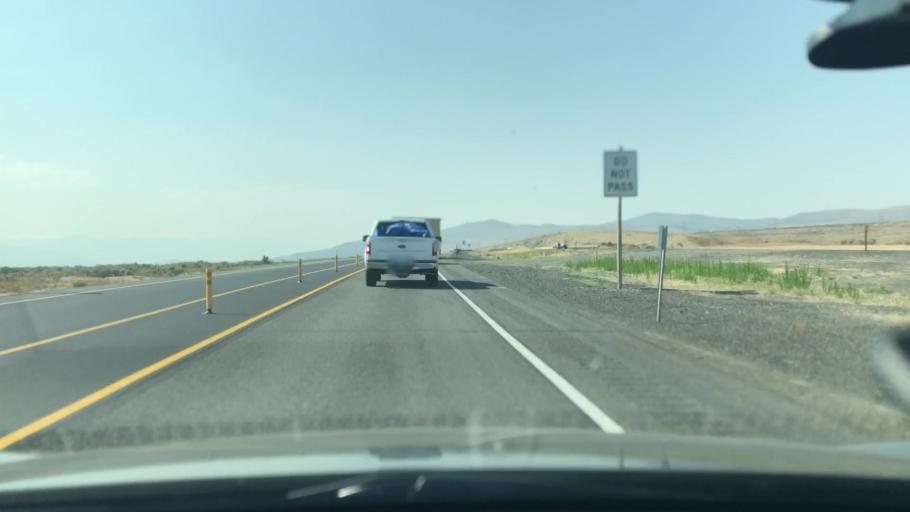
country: US
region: Oregon
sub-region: Baker County
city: Baker City
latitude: 44.6910
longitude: -117.6862
